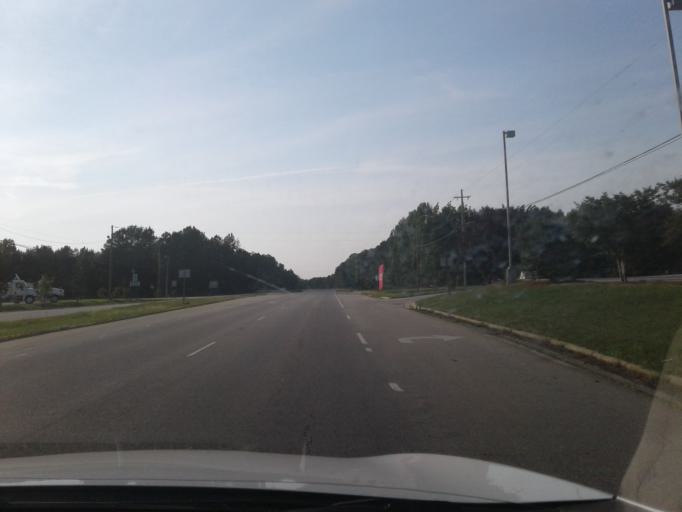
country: US
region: North Carolina
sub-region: Harnett County
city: Erwin
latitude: 35.3376
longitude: -78.6765
